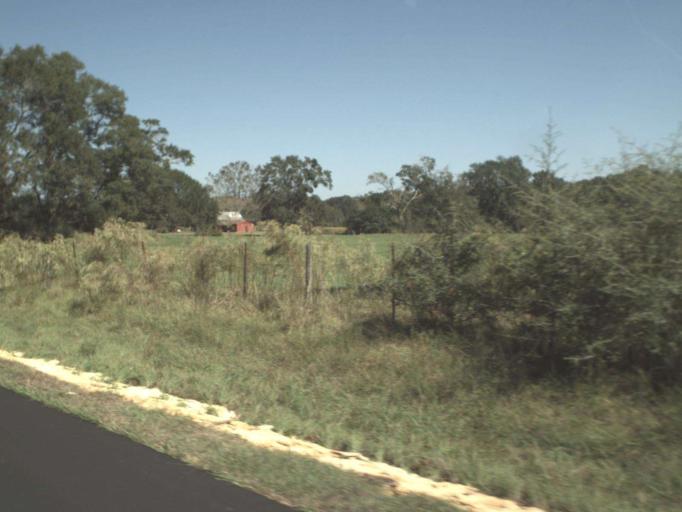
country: US
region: Alabama
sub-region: Covington County
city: Florala
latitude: 30.9175
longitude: -86.2811
